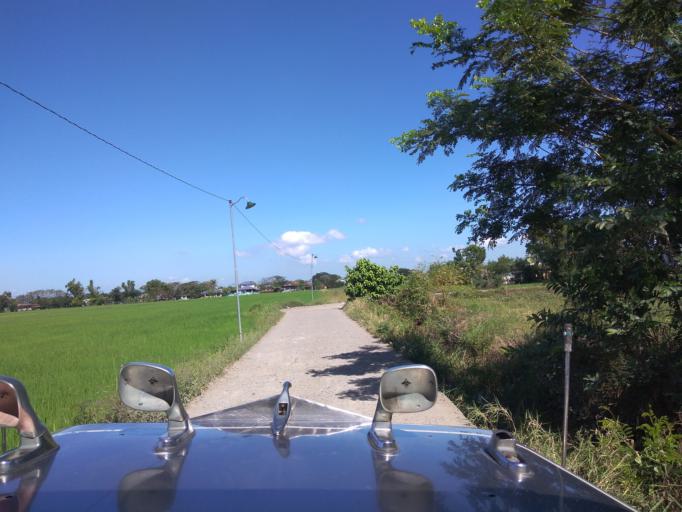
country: PH
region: Central Luzon
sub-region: Province of Pampanga
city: Batasan Bata
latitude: 15.1612
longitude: 120.9187
